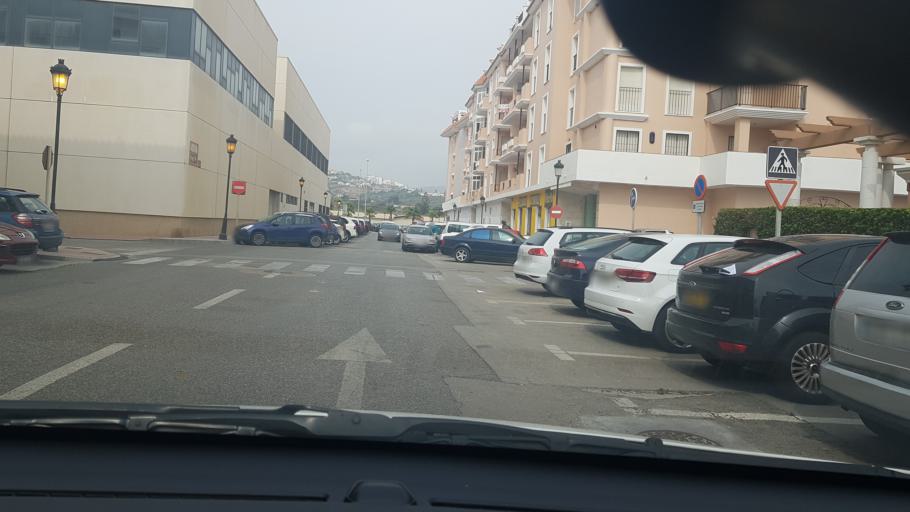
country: ES
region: Andalusia
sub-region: Provincia de Malaga
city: Manilva
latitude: 36.3700
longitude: -5.2247
